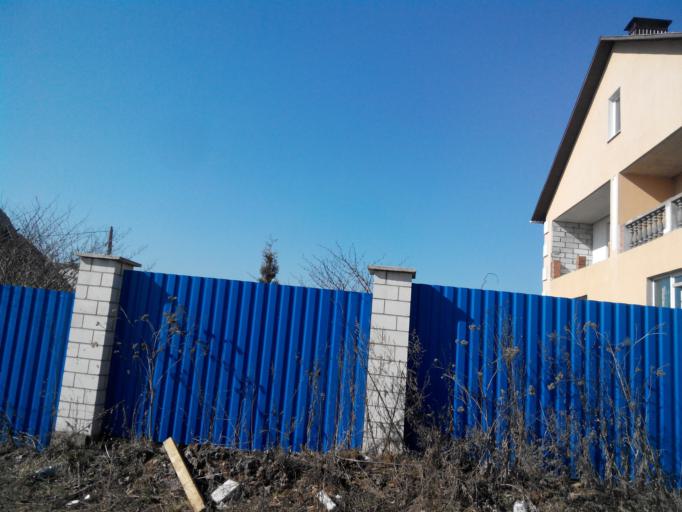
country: BY
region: Minsk
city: Zhdanovichy
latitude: 53.9153
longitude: 27.4017
